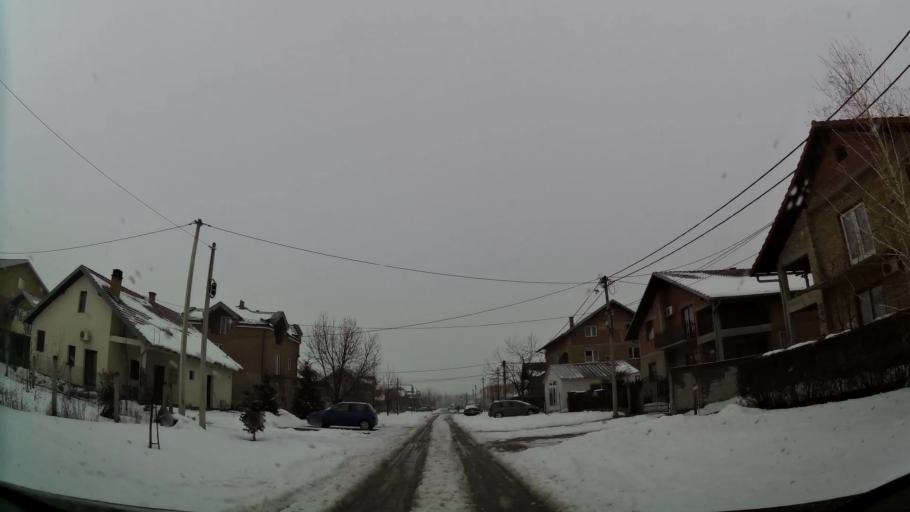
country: RS
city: Novi Banovci
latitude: 44.8785
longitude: 20.3189
